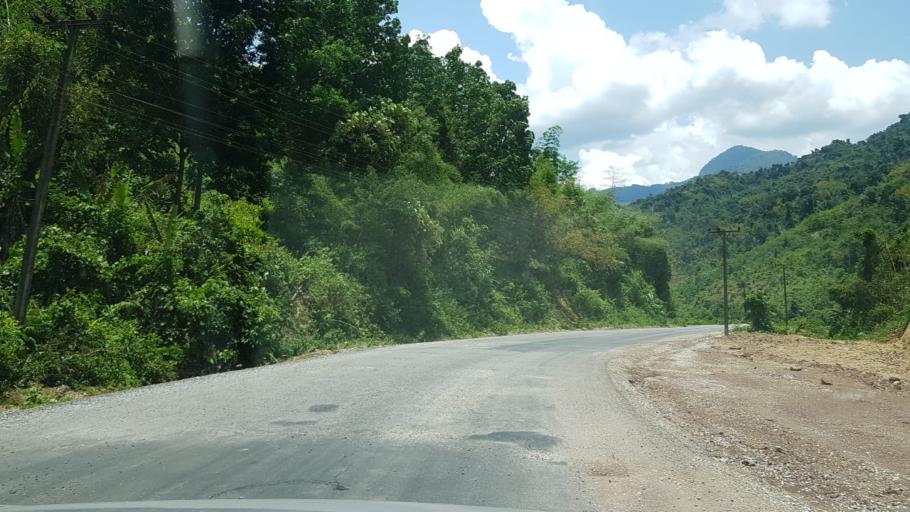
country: LA
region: Vientiane
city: Muang Kasi
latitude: 19.1297
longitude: 102.2372
